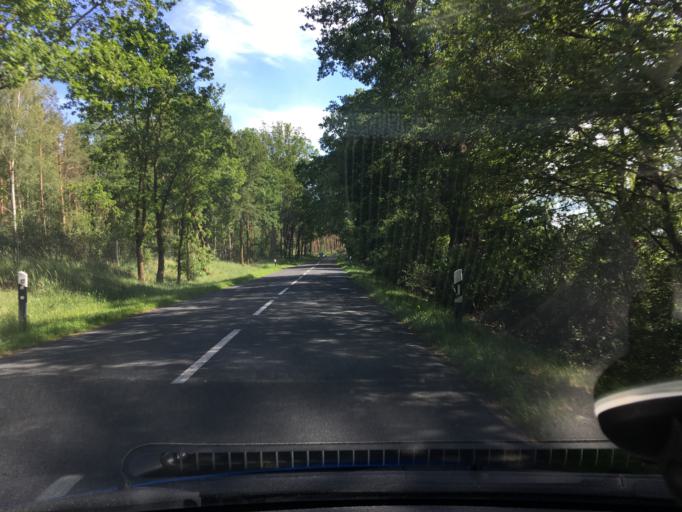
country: DE
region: Lower Saxony
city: Neu Darchau
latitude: 53.3017
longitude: 10.9303
